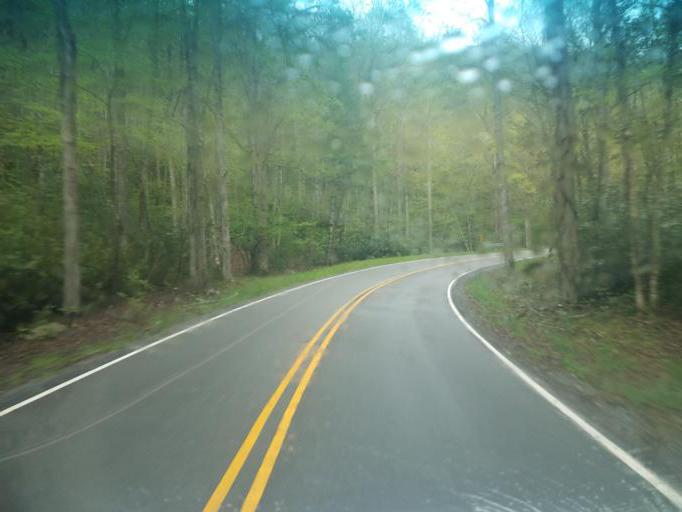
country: US
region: Virginia
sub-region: Washington County
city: Glade Spring
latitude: 36.6458
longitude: -81.7350
